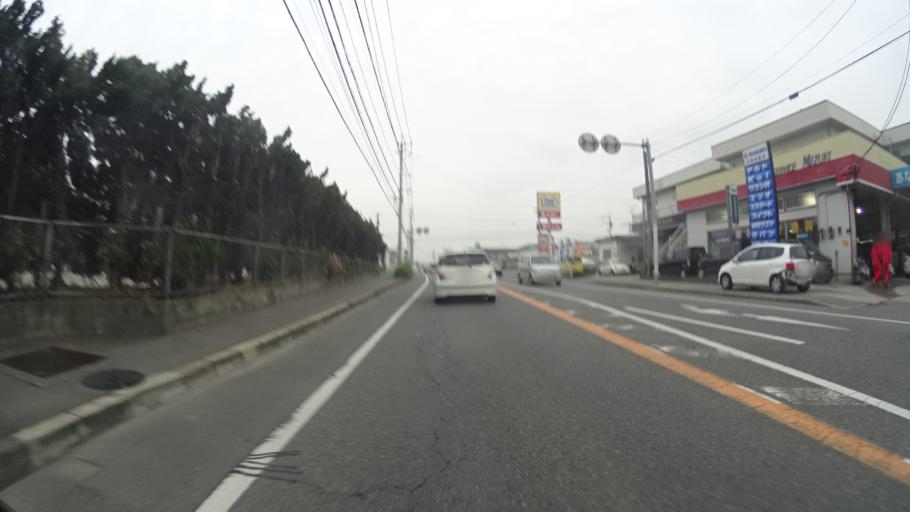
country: JP
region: Fukuoka
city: Dazaifu
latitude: 33.5159
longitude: 130.5046
